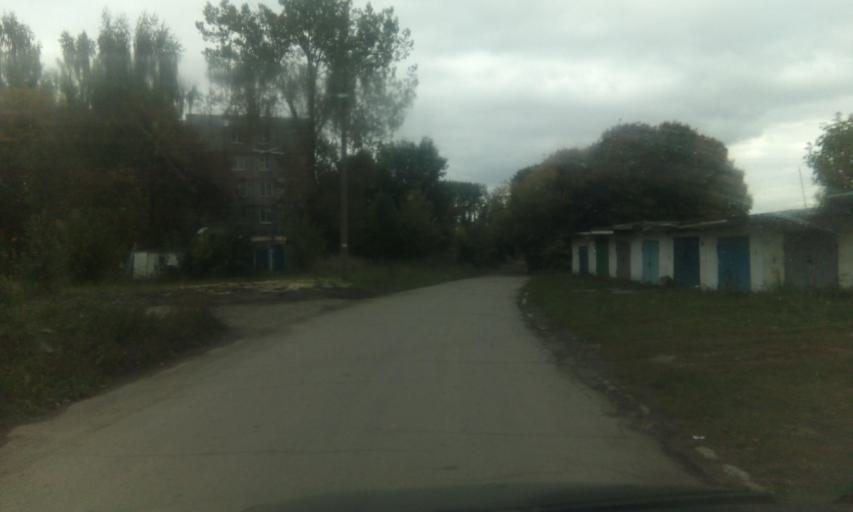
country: RU
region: Tula
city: Gritsovskiy
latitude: 54.1357
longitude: 38.1564
